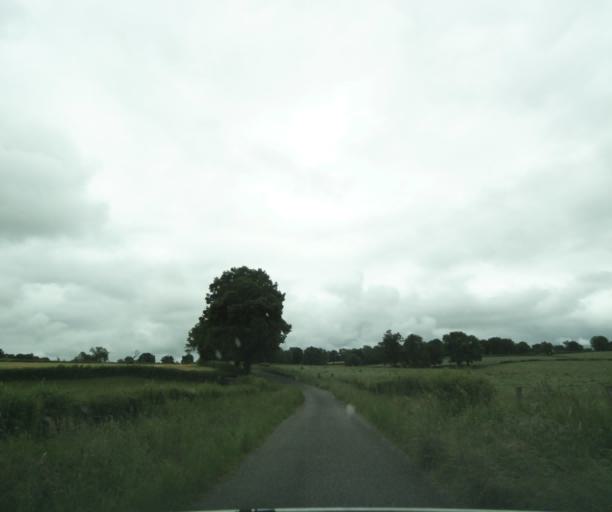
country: FR
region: Bourgogne
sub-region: Departement de Saone-et-Loire
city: Charolles
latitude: 46.4587
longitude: 4.3345
